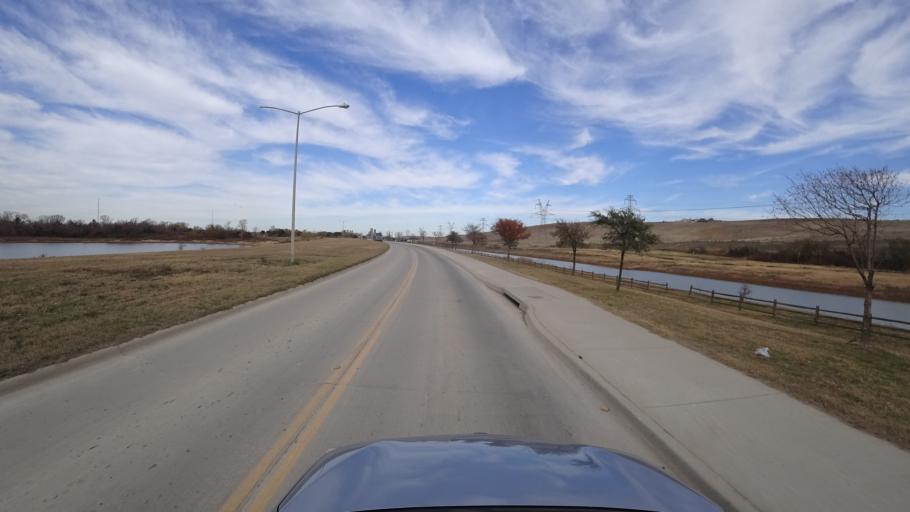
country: US
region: Texas
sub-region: Denton County
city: Lewisville
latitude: 33.0157
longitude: -96.9592
